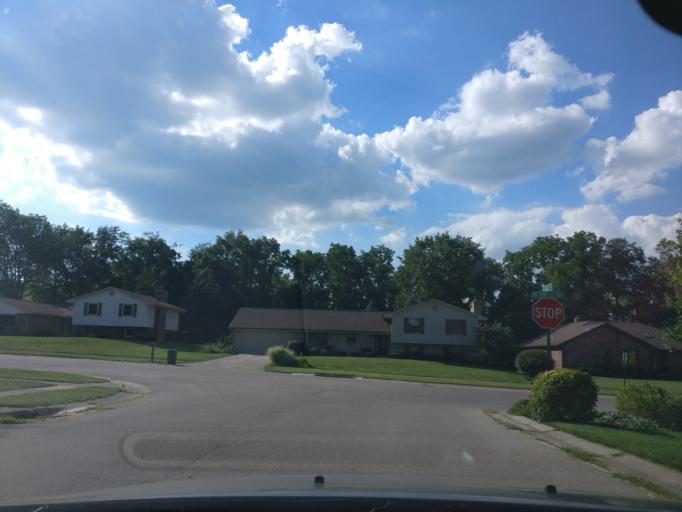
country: US
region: Ohio
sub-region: Warren County
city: Springboro
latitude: 39.5756
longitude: -84.2440
